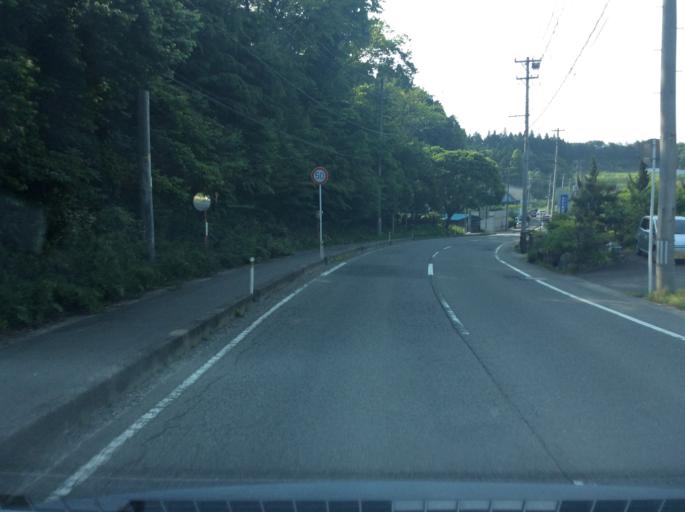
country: JP
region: Fukushima
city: Ishikawa
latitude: 37.1119
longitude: 140.2276
